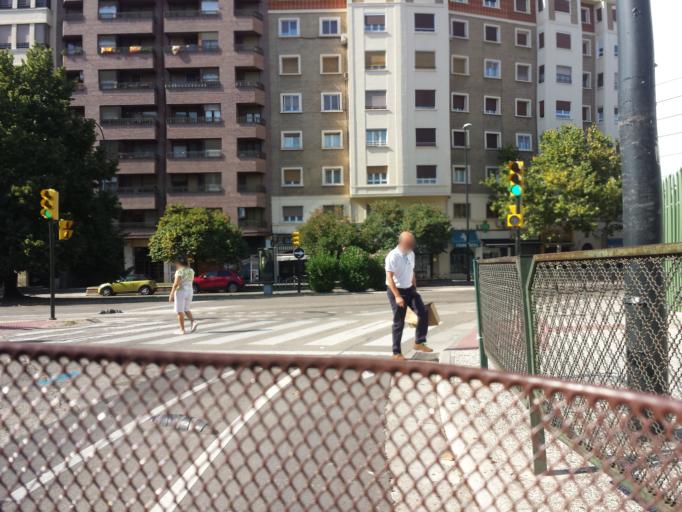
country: ES
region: Aragon
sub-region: Provincia de Zaragoza
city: Zaragoza
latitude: 41.6468
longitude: -0.8789
